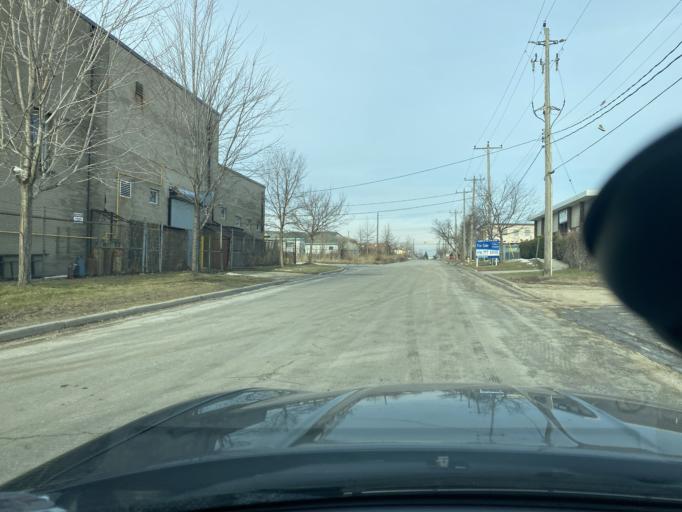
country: CA
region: Ontario
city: Scarborough
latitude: 43.7209
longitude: -79.2811
